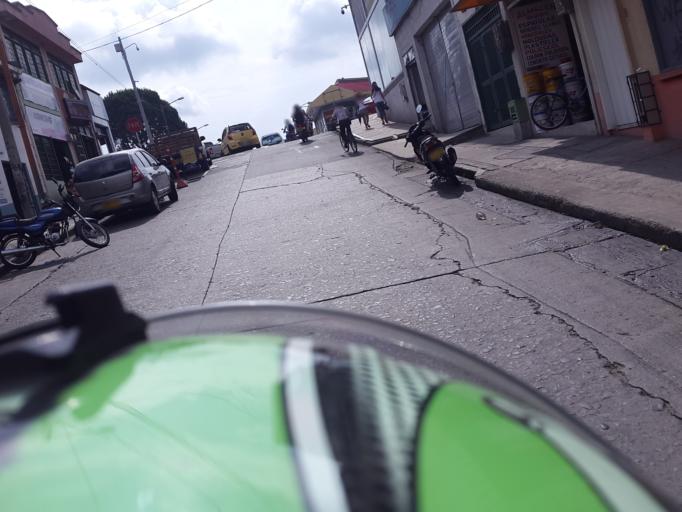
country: CO
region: Quindio
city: Armenia
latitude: 4.5380
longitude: -75.6752
